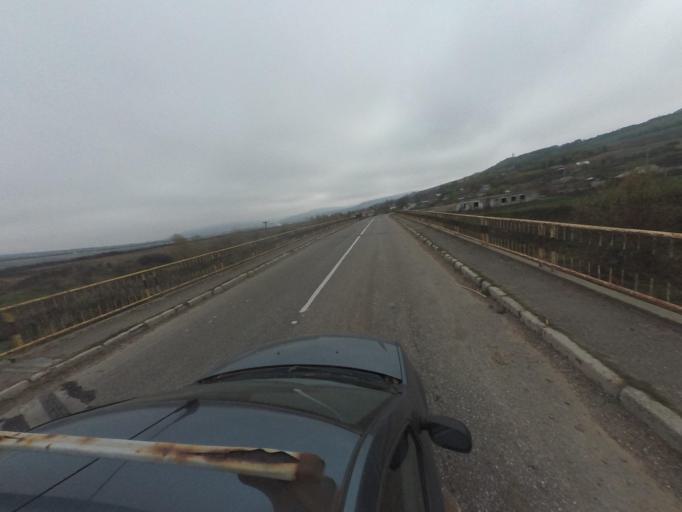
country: RO
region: Vaslui
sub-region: Comuna Bacesti
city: Bacesti
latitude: 46.8381
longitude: 27.2271
